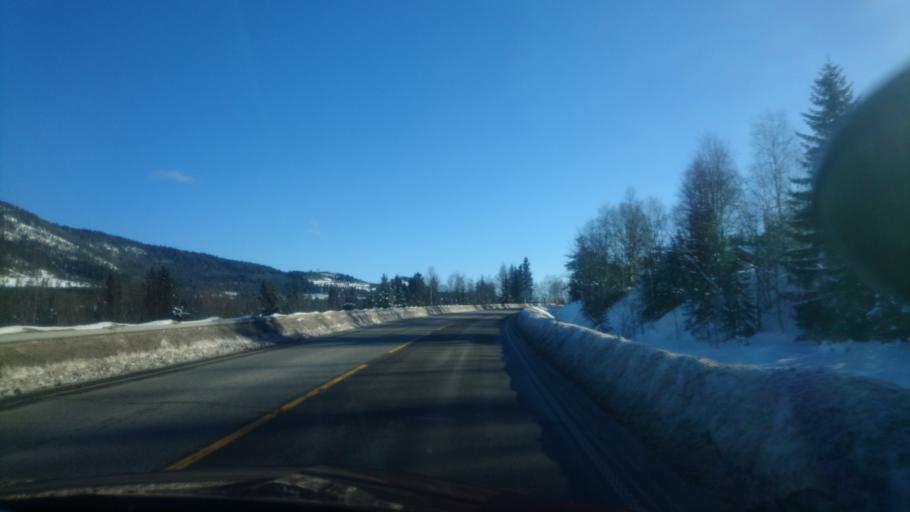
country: NO
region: Hedmark
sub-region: Trysil
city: Innbygda
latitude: 61.2701
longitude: 12.3018
